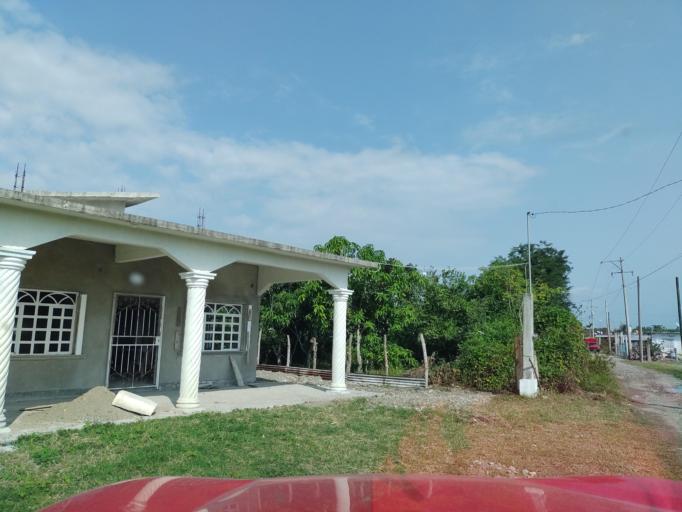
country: MX
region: Puebla
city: Espinal
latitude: 20.2778
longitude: -97.3327
